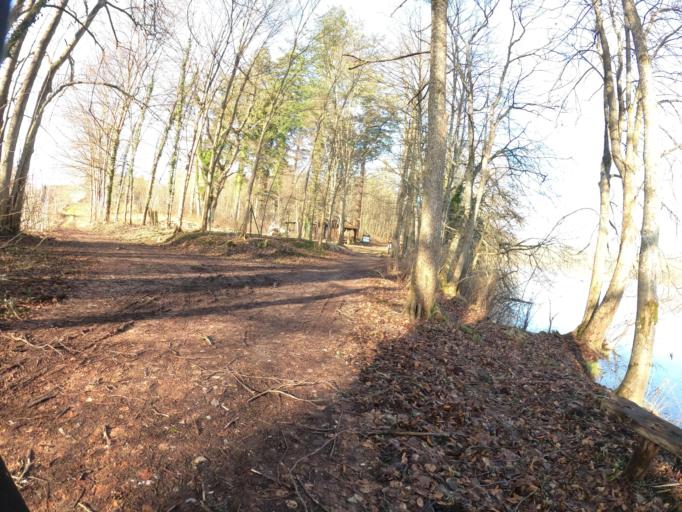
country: PL
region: West Pomeranian Voivodeship
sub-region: Powiat koszalinski
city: Polanow
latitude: 54.2135
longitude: 16.6959
